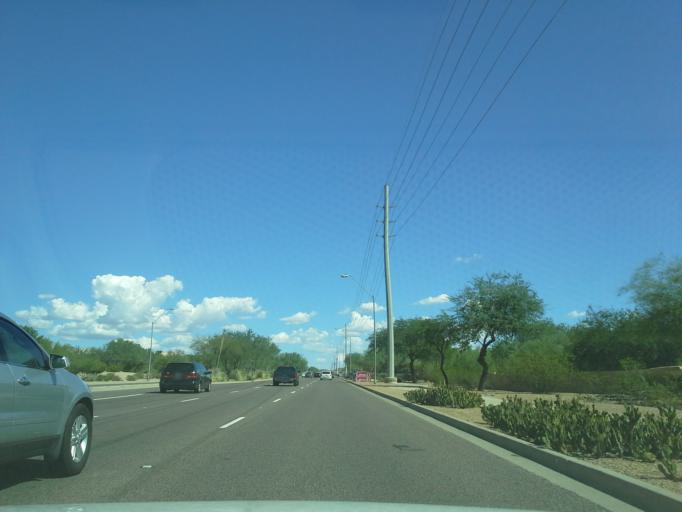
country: US
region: Arizona
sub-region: Maricopa County
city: Scottsdale
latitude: 33.5823
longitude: -111.8263
